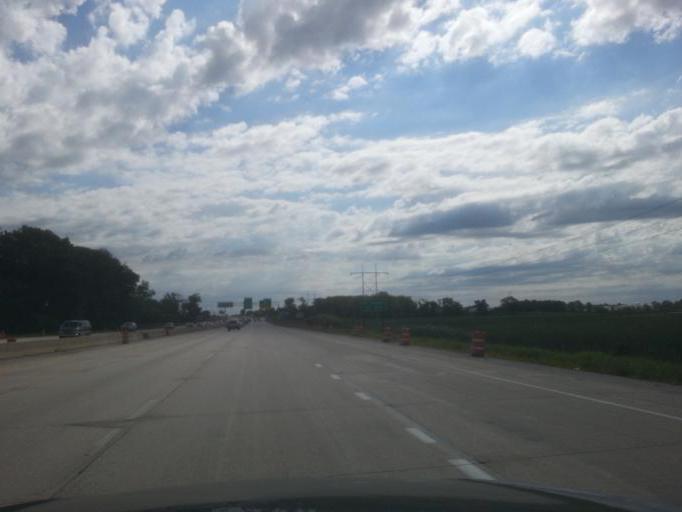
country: US
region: Wisconsin
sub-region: Dane County
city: Monona
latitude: 43.0449
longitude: -89.3198
